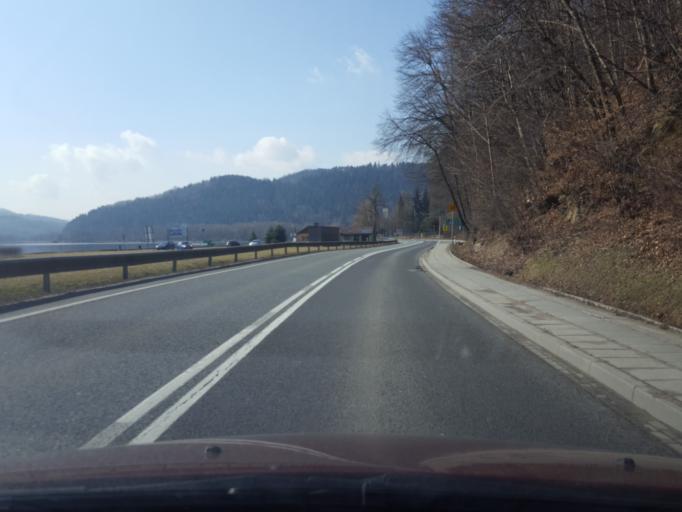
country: PL
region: Lesser Poland Voivodeship
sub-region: Powiat brzeski
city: Czchow
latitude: 49.8043
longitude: 20.6527
